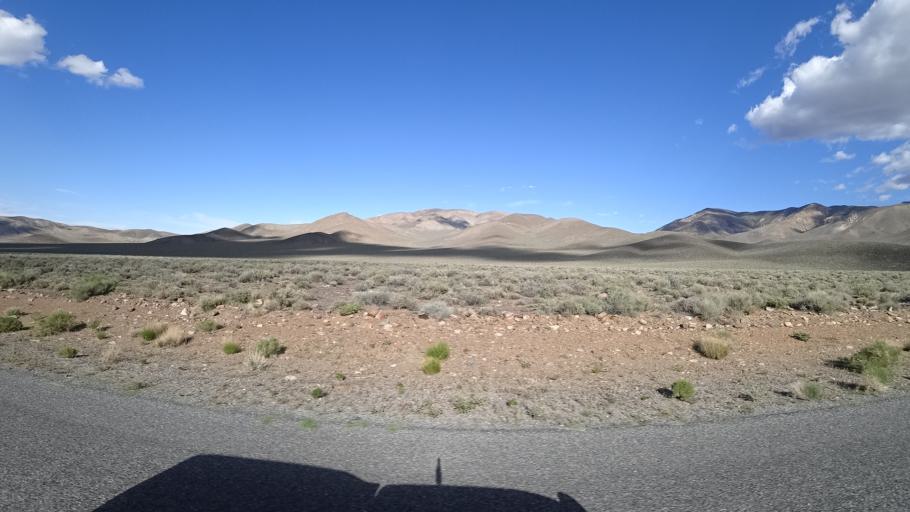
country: US
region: California
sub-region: San Bernardino County
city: Searles Valley
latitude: 36.3409
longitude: -117.1356
